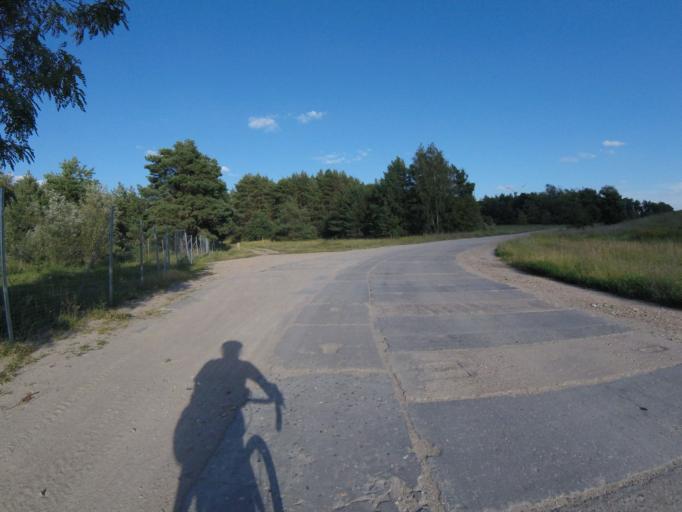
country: DE
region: Brandenburg
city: Zossen
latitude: 52.2162
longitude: 13.4781
